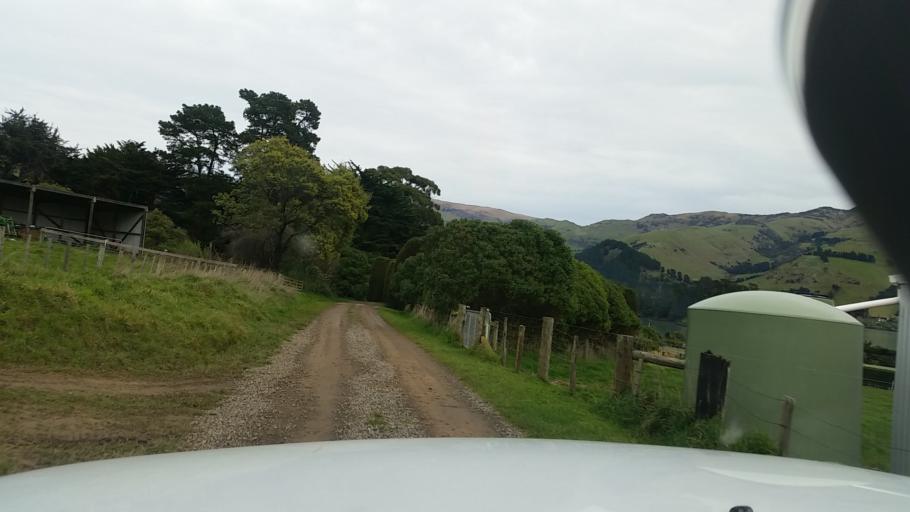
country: NZ
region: Canterbury
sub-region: Christchurch City
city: Christchurch
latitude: -43.6489
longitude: 172.8402
